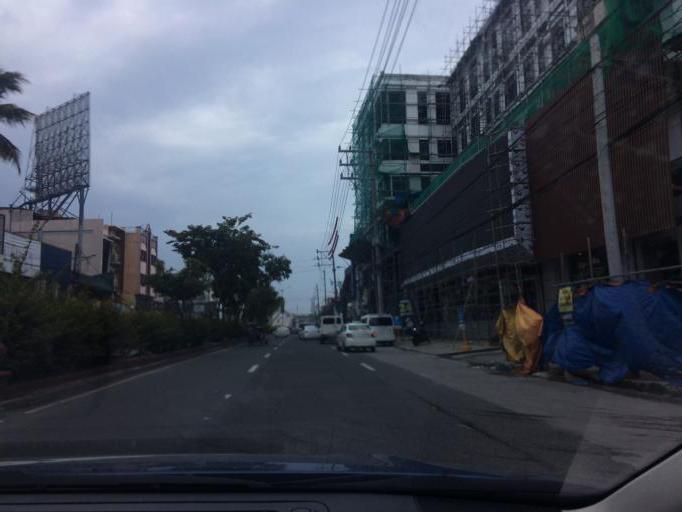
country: PH
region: Metro Manila
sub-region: Makati City
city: Makati City
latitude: 14.5338
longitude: 121.0036
